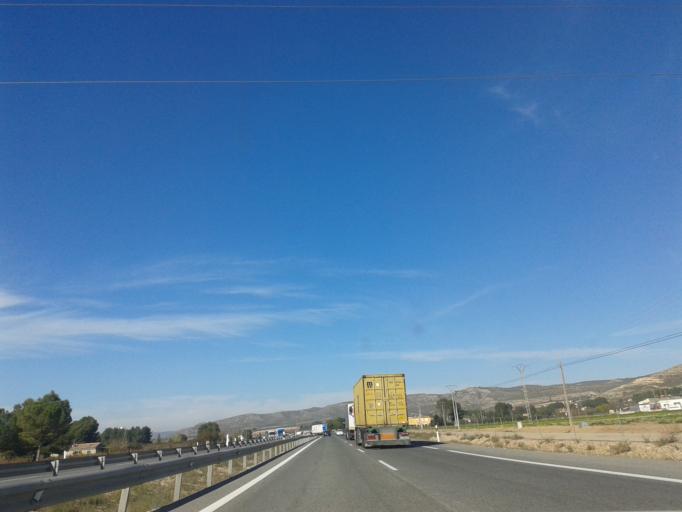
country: ES
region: Valencia
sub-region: Provincia de Alicante
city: Villena
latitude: 38.6628
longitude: -0.8796
